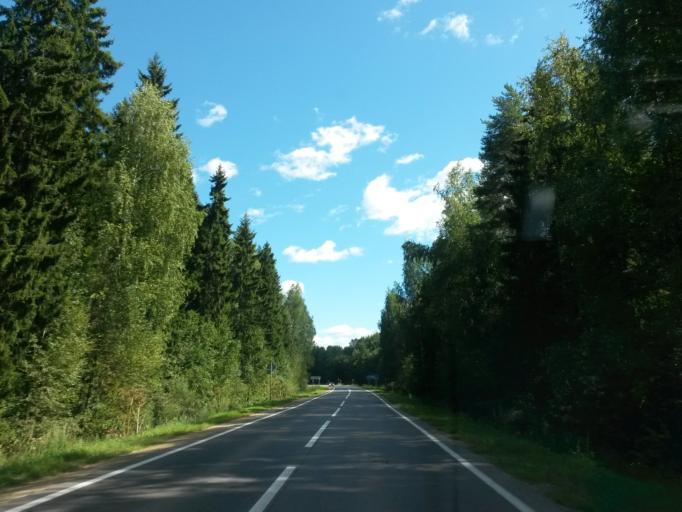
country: RU
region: Jaroslavl
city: Yaroslavl
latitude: 57.8005
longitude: 39.7963
